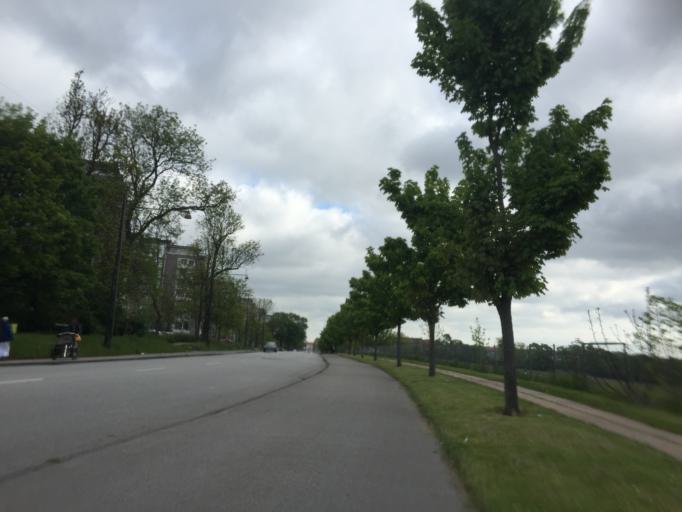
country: DK
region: Capital Region
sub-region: Kobenhavn
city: Vanlose
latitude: 55.7020
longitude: 12.5121
